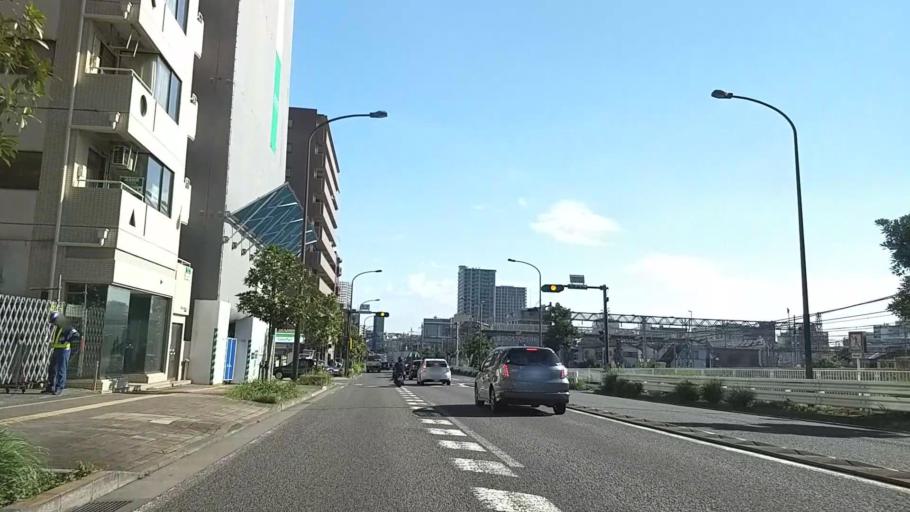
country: JP
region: Kanagawa
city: Yokohama
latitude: 35.4735
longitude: 139.6285
